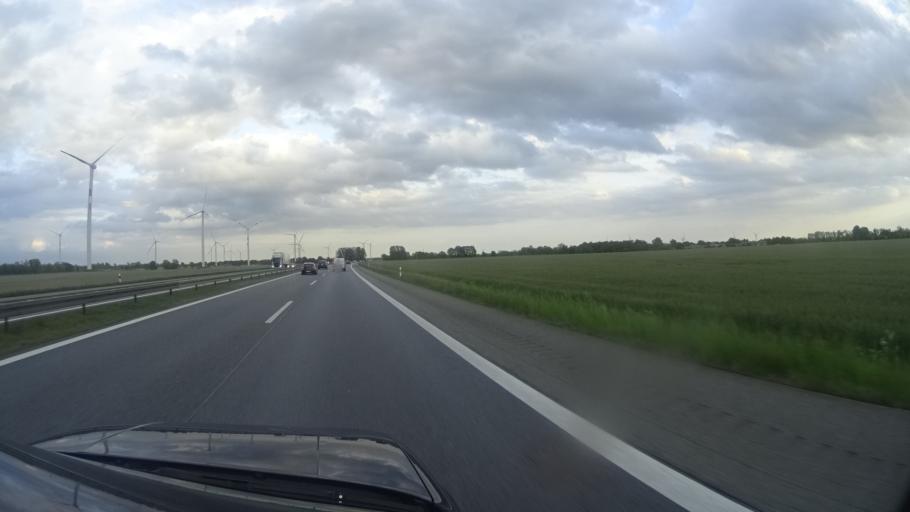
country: DE
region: Brandenburg
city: Dabergotz
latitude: 52.9308
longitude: 12.7032
